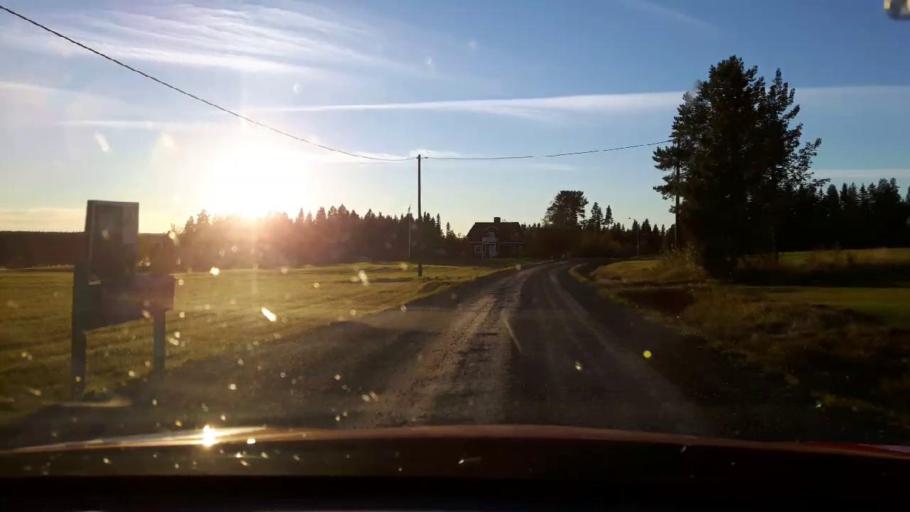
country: SE
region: Jaemtland
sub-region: Krokoms Kommun
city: Krokom
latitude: 63.4266
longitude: 14.4546
